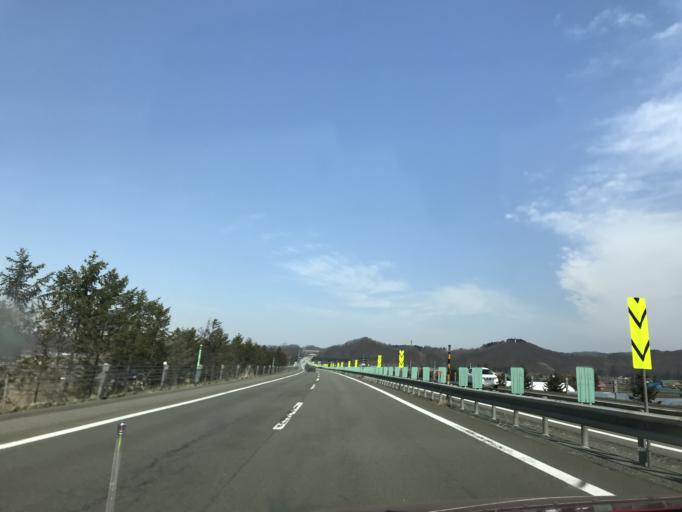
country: JP
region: Hokkaido
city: Iwamizawa
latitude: 43.2279
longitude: 141.8305
